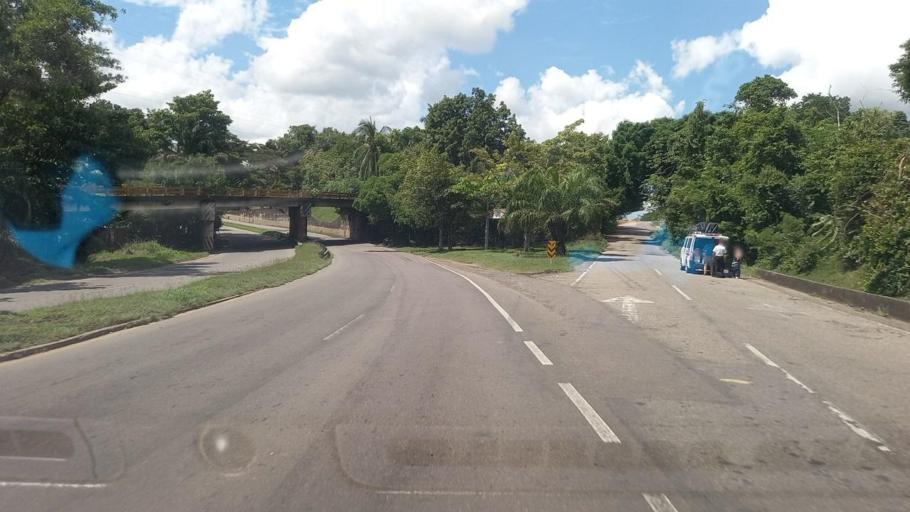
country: CO
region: Santander
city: Barrancabermeja
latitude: 7.1191
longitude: -73.6147
